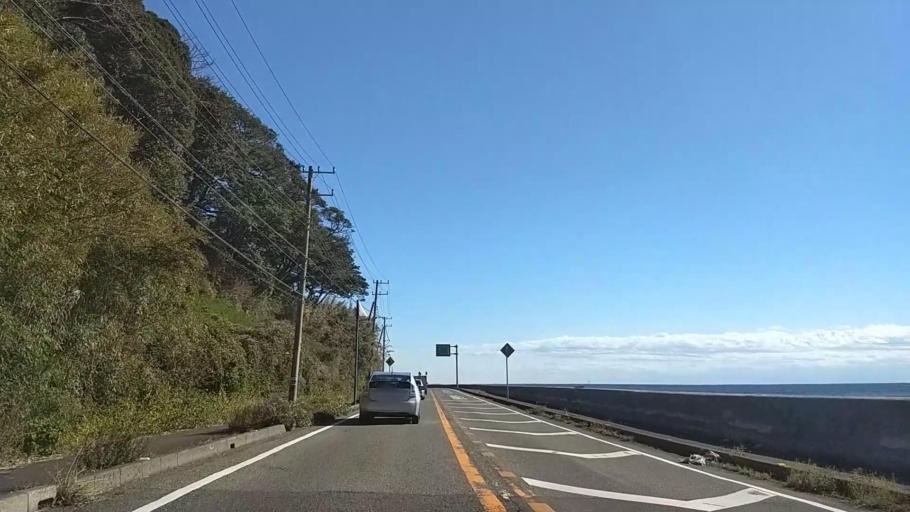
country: JP
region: Chiba
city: Kawaguchi
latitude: 35.0742
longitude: 140.0862
